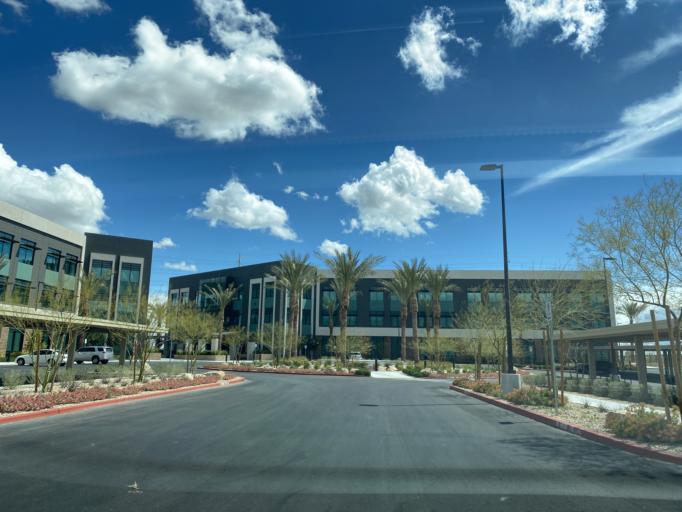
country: US
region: Nevada
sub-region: Clark County
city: Summerlin South
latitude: 36.1170
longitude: -115.3173
